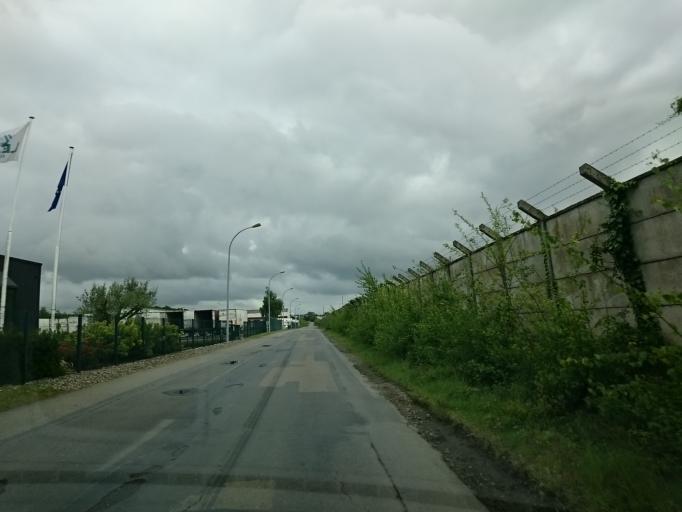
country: FR
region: Brittany
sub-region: Departement d'Ille-et-Vilaine
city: Vern-sur-Seiche
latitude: 48.0593
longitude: -1.6092
